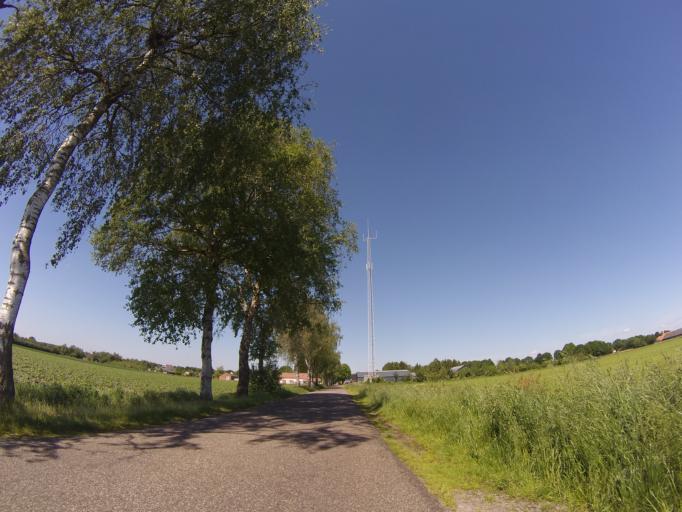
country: NL
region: Drenthe
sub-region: Gemeente Hoogeveen
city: Hoogeveen
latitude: 52.7646
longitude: 6.6135
